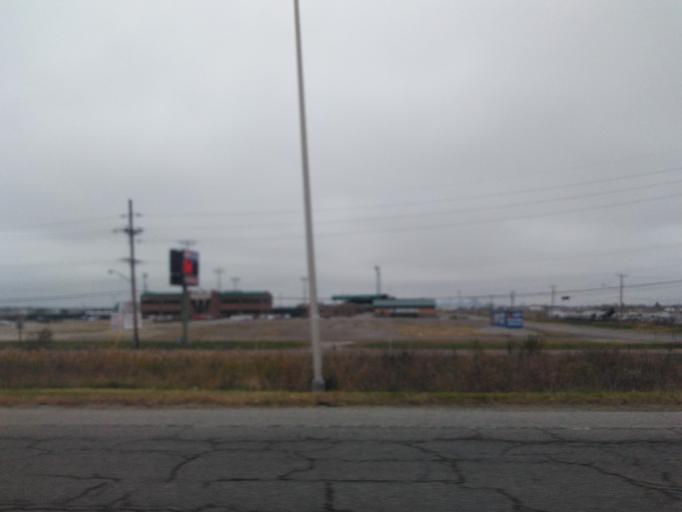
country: US
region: Illinois
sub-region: Saint Clair County
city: Centreville
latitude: 38.5641
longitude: -90.1326
